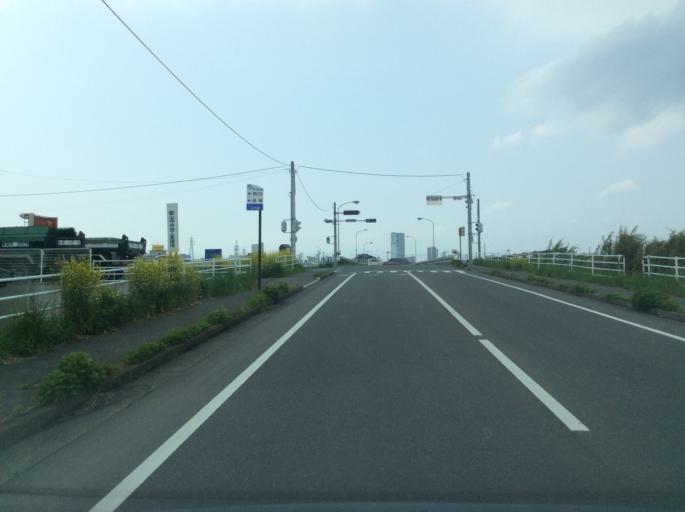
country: JP
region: Fukushima
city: Koriyama
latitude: 37.3855
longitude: 140.4025
